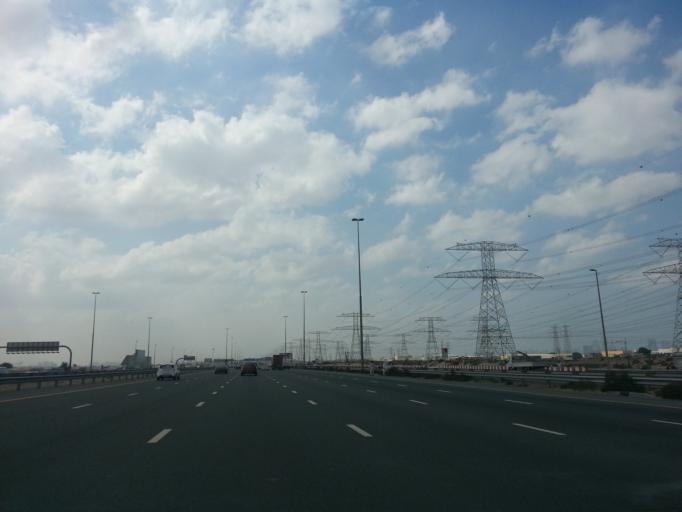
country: AE
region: Dubai
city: Dubai
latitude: 25.1171
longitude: 55.2462
